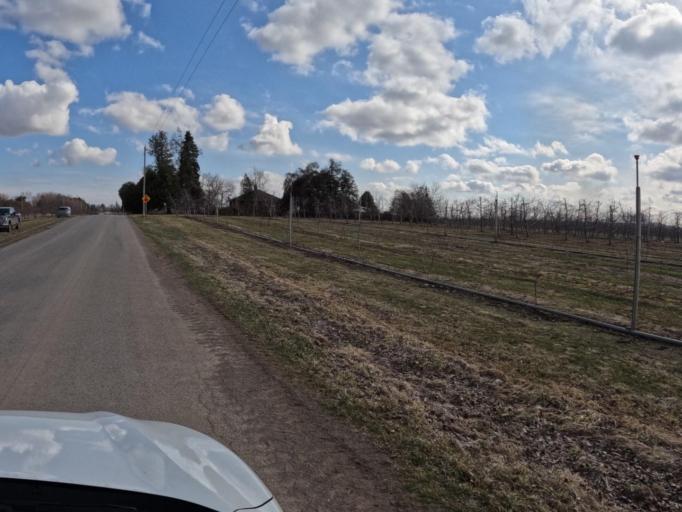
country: CA
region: Ontario
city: Norfolk County
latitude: 42.8784
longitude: -80.2810
